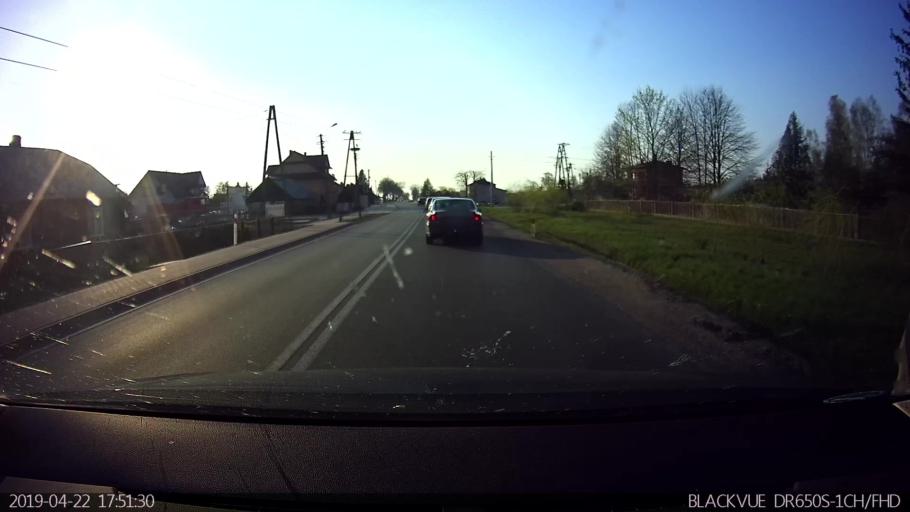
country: PL
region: Masovian Voivodeship
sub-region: Powiat wegrowski
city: Wegrow
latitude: 52.4354
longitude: 21.9930
